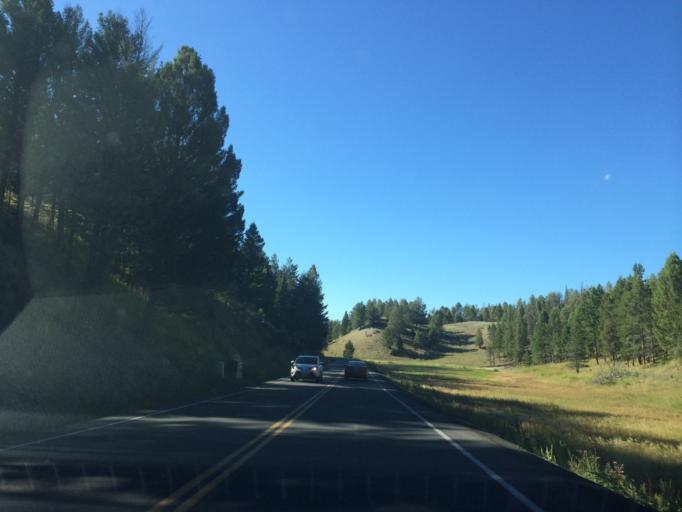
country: US
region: Montana
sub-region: Gallatin County
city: West Yellowstone
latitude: 44.9071
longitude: -110.4008
